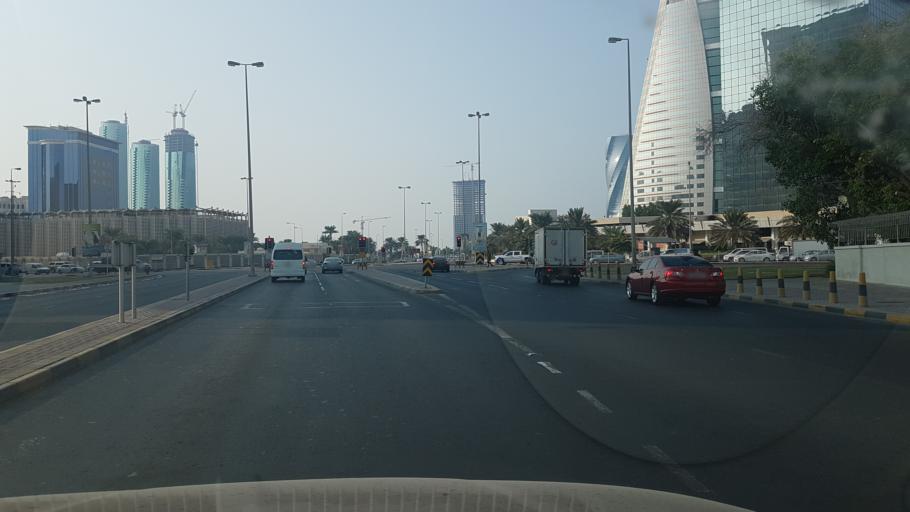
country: BH
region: Manama
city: Manama
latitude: 26.2368
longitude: 50.5821
